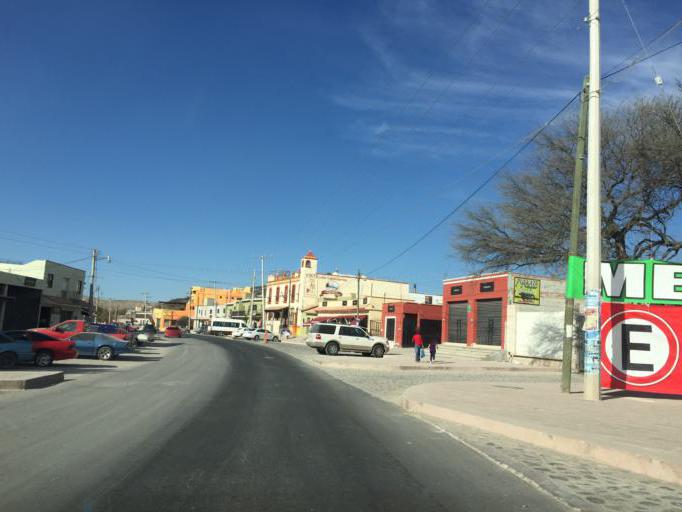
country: MX
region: Queretaro
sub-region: Ezequiel Montes
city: San Jose del Jagueey
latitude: 20.7345
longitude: -99.9373
